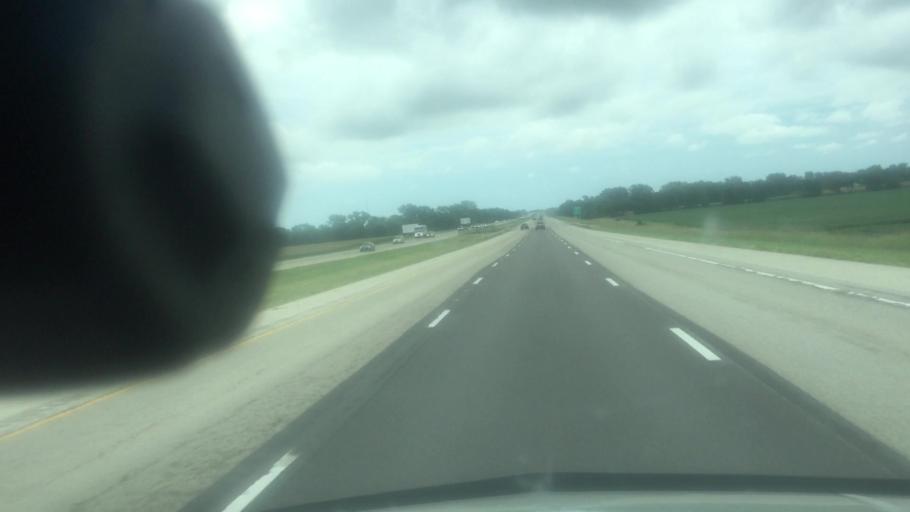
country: US
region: Illinois
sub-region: Logan County
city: Lincoln
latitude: 40.1374
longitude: -89.4173
